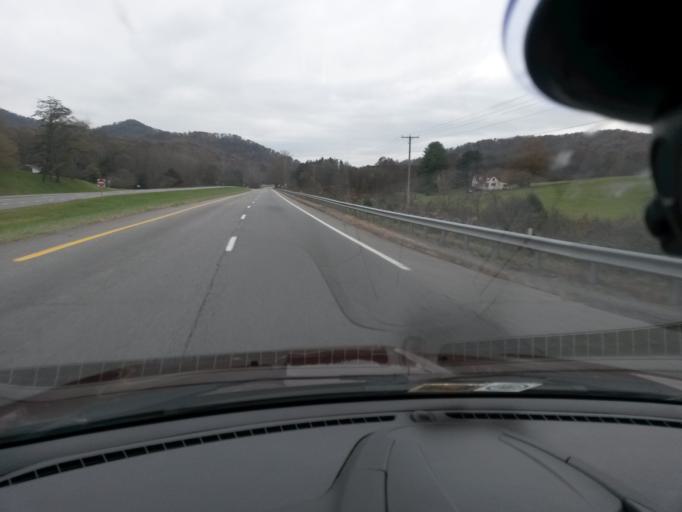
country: US
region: Virginia
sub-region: Albemarle County
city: Crozet
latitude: 37.9006
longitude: -78.6949
